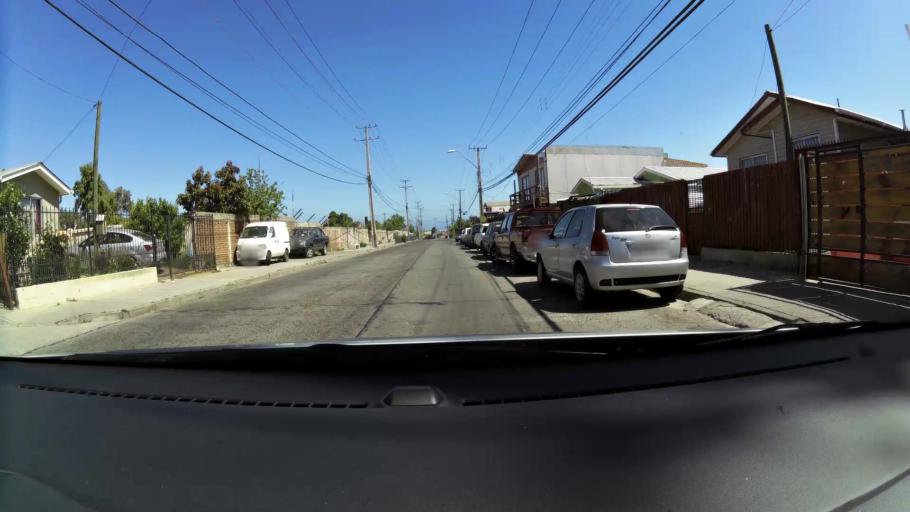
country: CL
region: Valparaiso
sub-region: Provincia de Valparaiso
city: Vina del Mar
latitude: -33.0520
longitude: -71.5839
